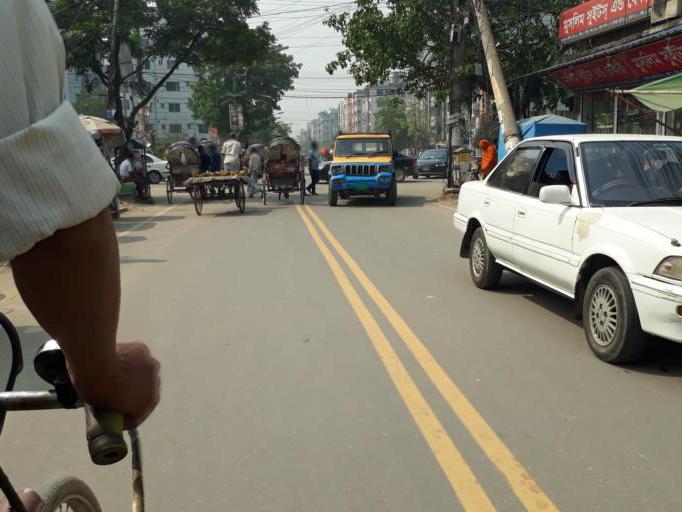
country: BD
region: Dhaka
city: Tungi
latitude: 23.8746
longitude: 90.3840
